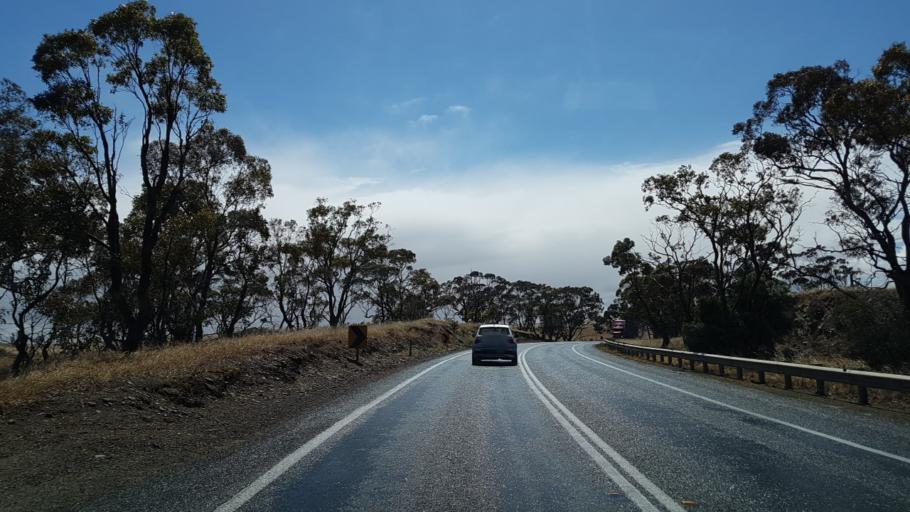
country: AU
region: South Australia
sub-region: Barossa
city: Angaston
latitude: -34.4000
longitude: 139.1708
